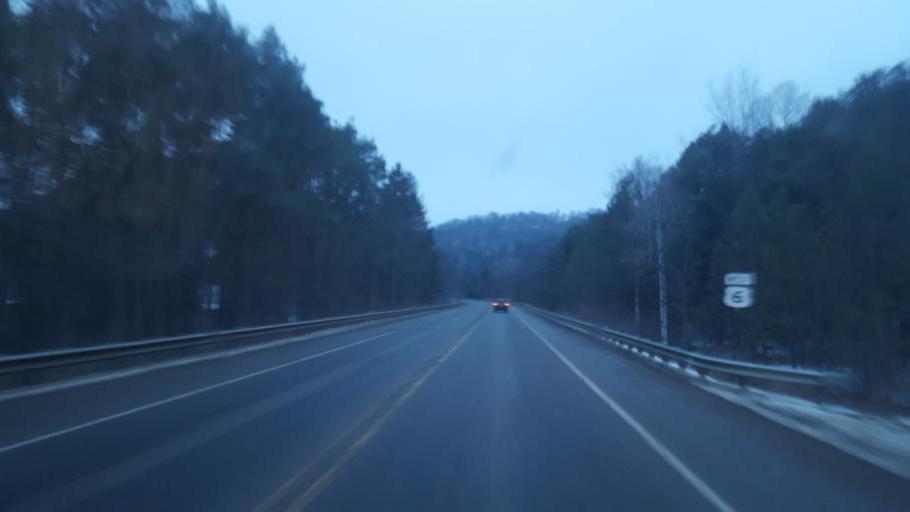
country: US
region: Pennsylvania
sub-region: Potter County
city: Coudersport
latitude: 41.7796
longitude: -78.1454
